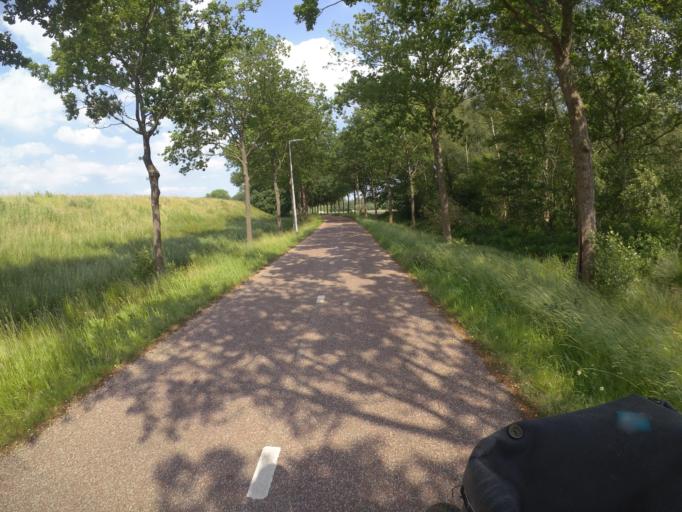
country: NL
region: Drenthe
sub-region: Gemeente Assen
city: Assen
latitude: 52.9819
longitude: 6.5230
